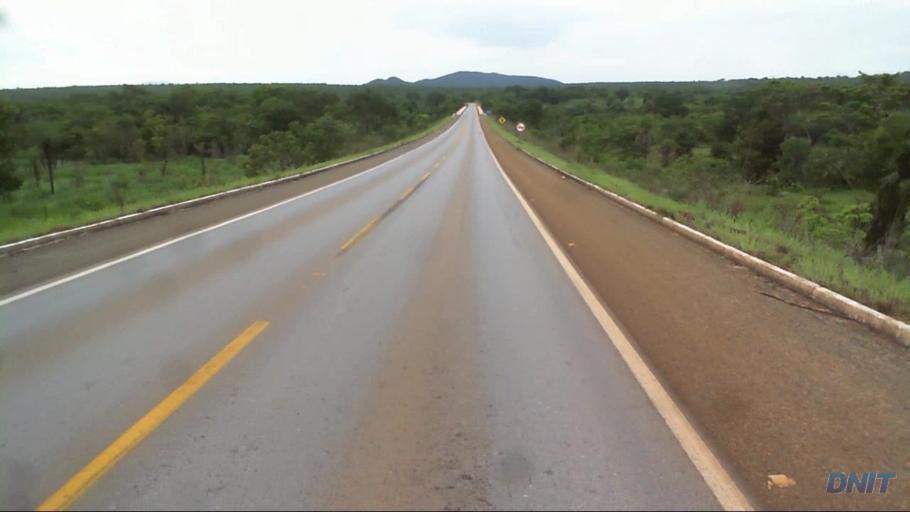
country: BR
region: Goias
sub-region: Uruacu
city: Uruacu
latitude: -14.7456
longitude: -49.0780
